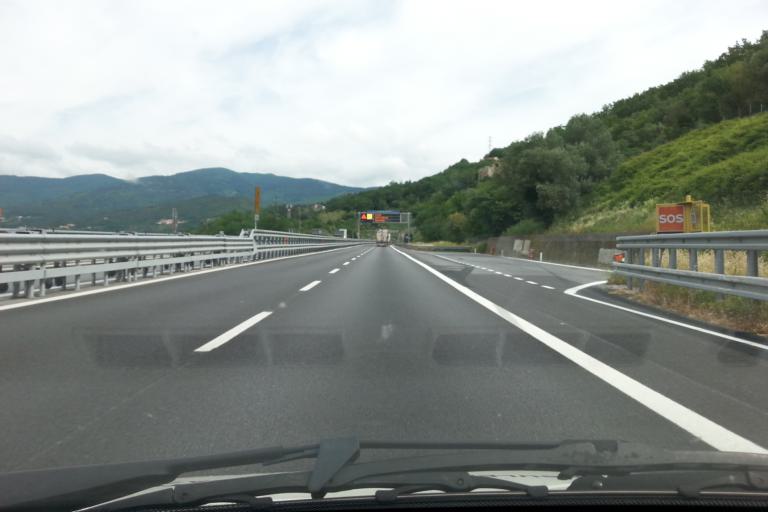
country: IT
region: Liguria
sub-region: Provincia di Savona
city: Calice Ligure
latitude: 44.1943
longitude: 8.3058
